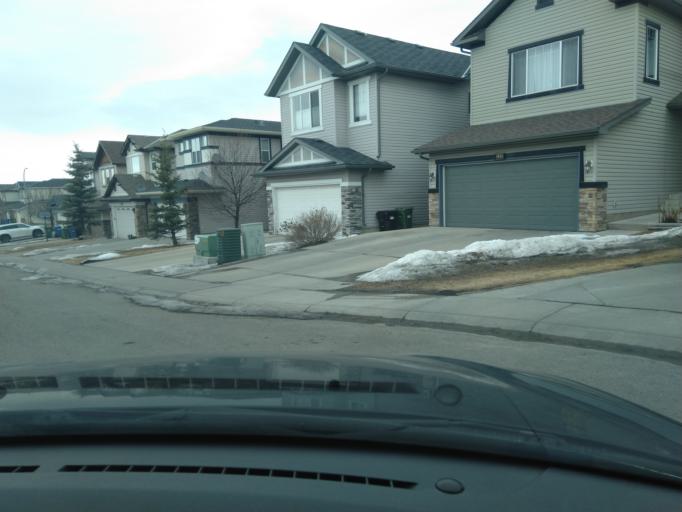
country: CA
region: Alberta
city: Calgary
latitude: 51.1575
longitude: -114.0877
